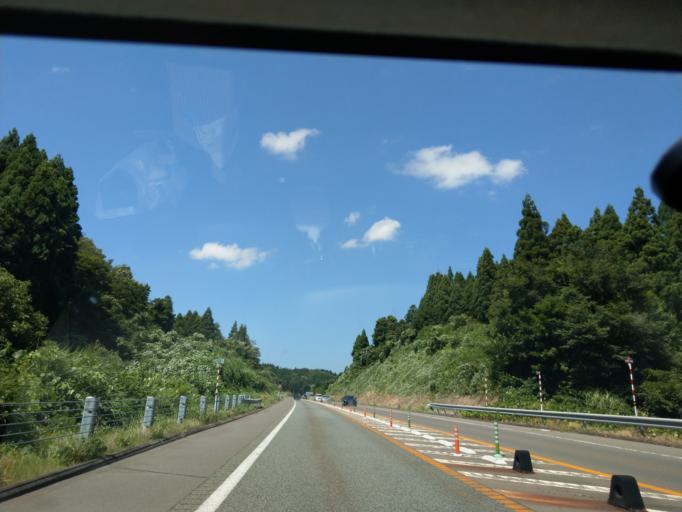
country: JP
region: Akita
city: Akita
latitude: 39.6719
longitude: 140.1877
